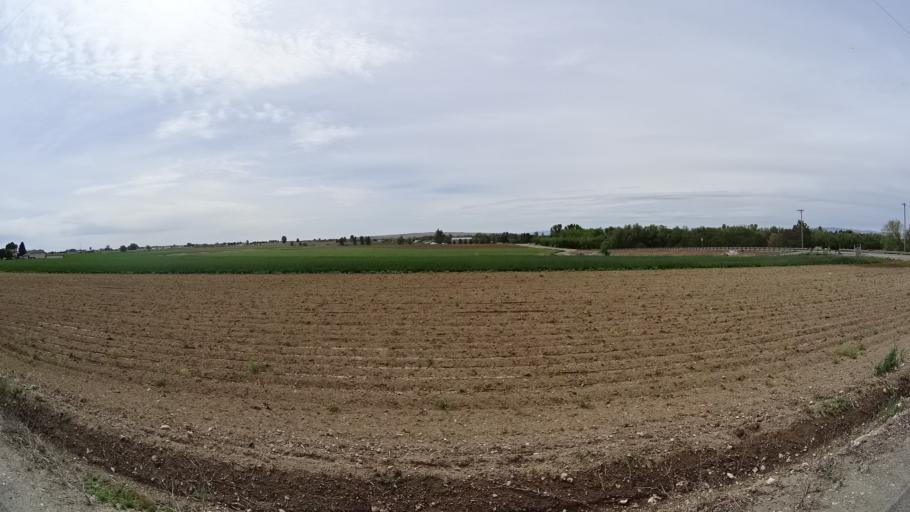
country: US
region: Idaho
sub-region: Ada County
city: Kuna
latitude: 43.5322
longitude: -116.4527
